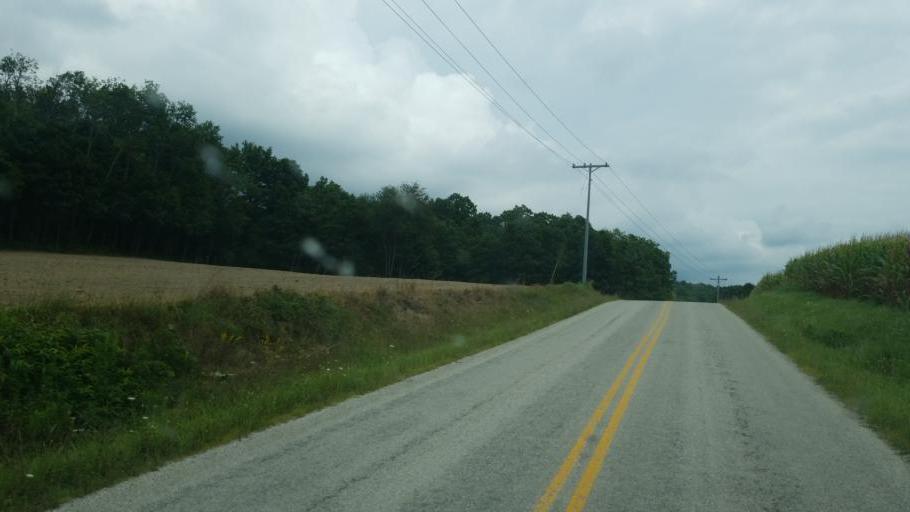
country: US
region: Ohio
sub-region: Ashland County
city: Loudonville
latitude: 40.5801
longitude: -82.3140
